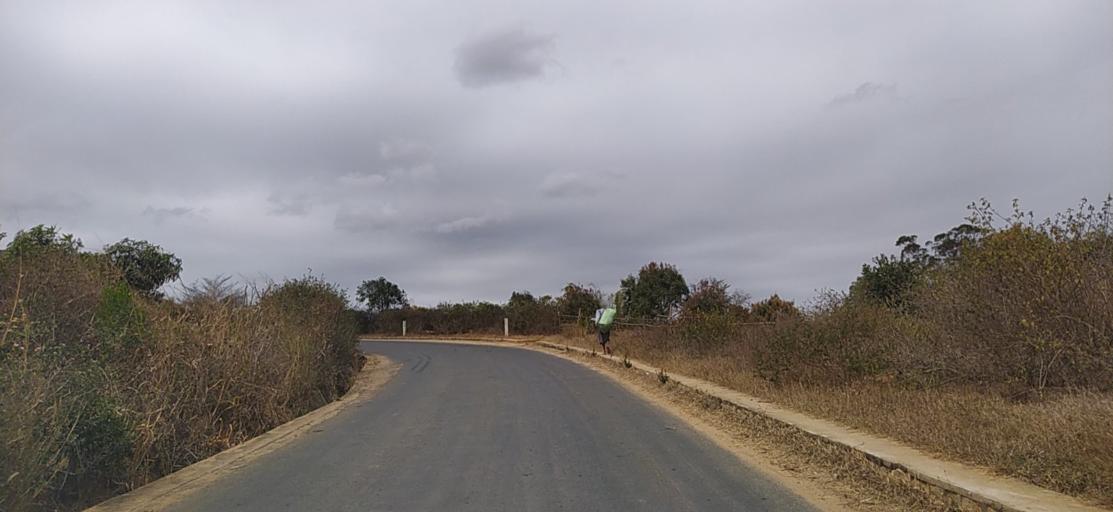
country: MG
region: Alaotra Mangoro
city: Ambatondrazaka
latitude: -17.9302
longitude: 48.2557
